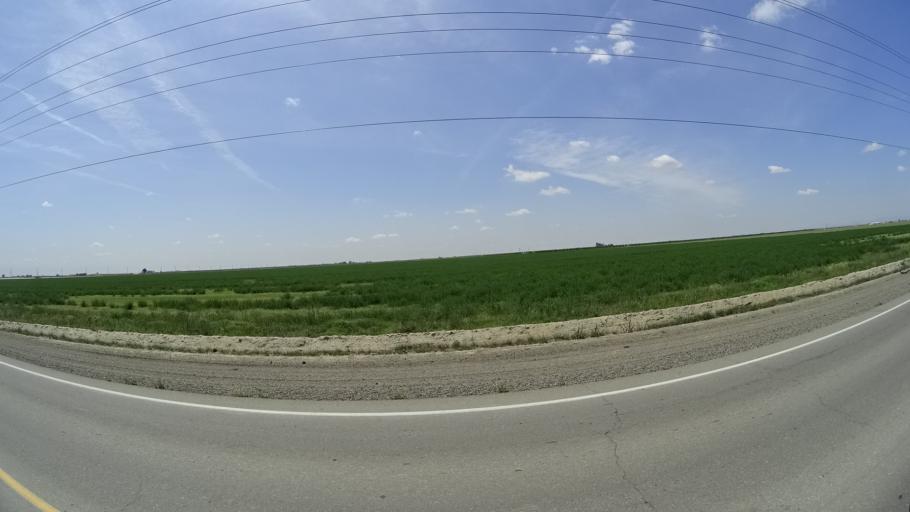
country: US
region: California
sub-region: Tulare County
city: Goshen
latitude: 36.2979
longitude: -119.4993
